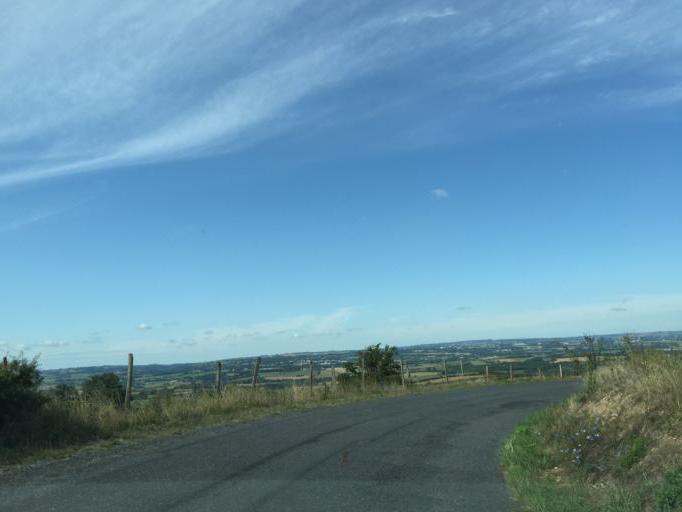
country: FR
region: Midi-Pyrenees
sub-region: Departement de l'Aveyron
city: Sainte-Radegonde
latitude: 44.3146
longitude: 2.6659
